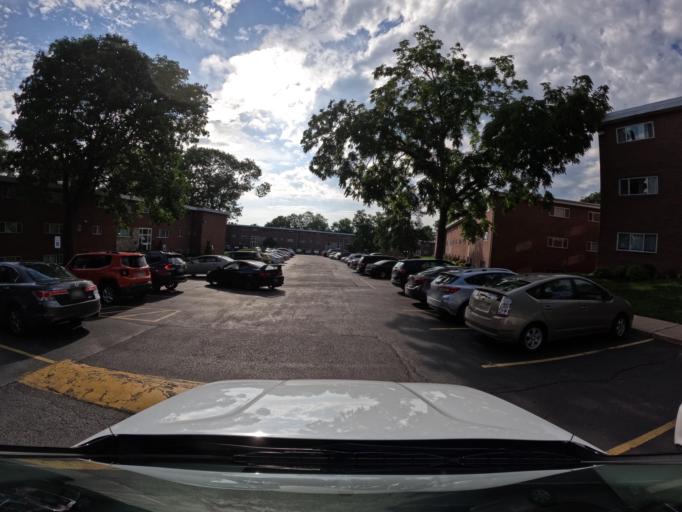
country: US
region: Maryland
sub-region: Baltimore County
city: Lutherville
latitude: 39.4197
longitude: -76.6310
